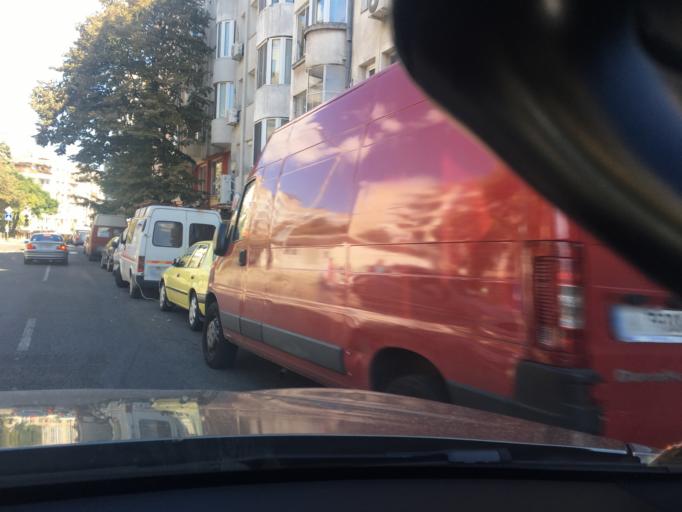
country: BG
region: Burgas
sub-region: Obshtina Burgas
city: Burgas
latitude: 42.5088
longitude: 27.4733
